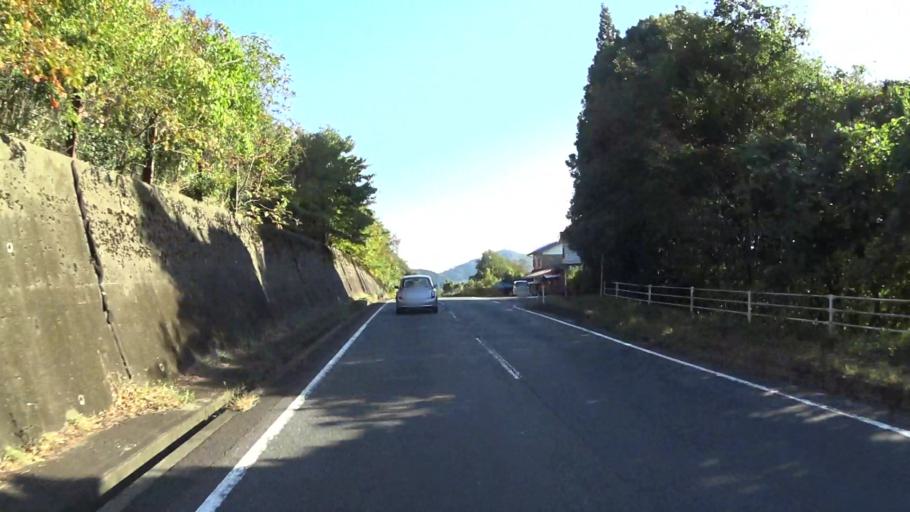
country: JP
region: Kyoto
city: Fukuchiyama
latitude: 35.3805
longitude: 135.0973
